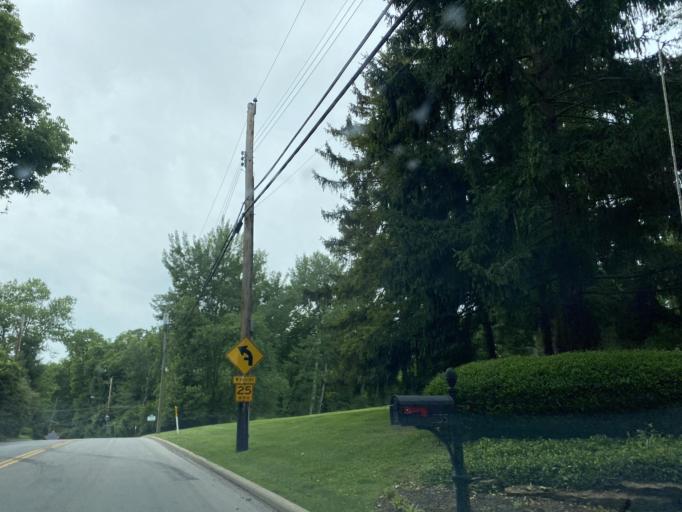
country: US
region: Ohio
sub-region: Hamilton County
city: Salem Heights
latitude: 39.0831
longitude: -84.4099
